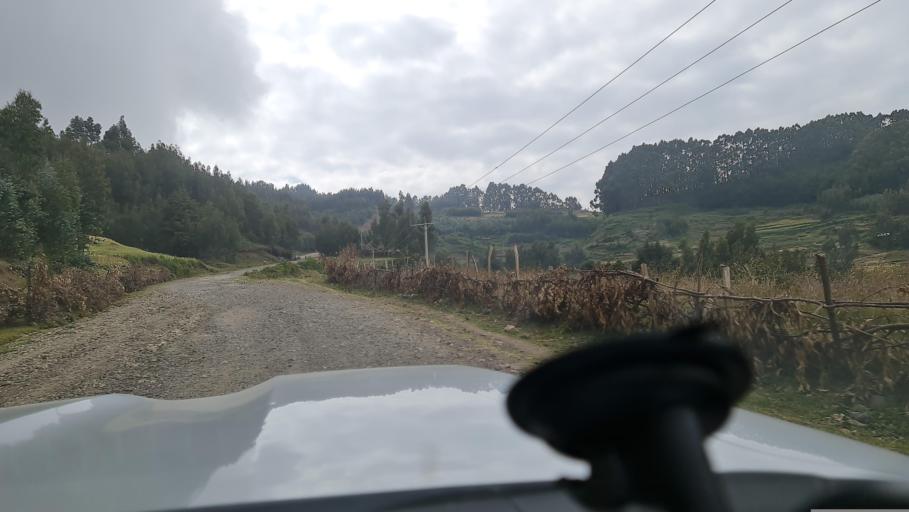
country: ET
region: Amhara
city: Abomsa
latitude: 10.1351
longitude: 39.7893
